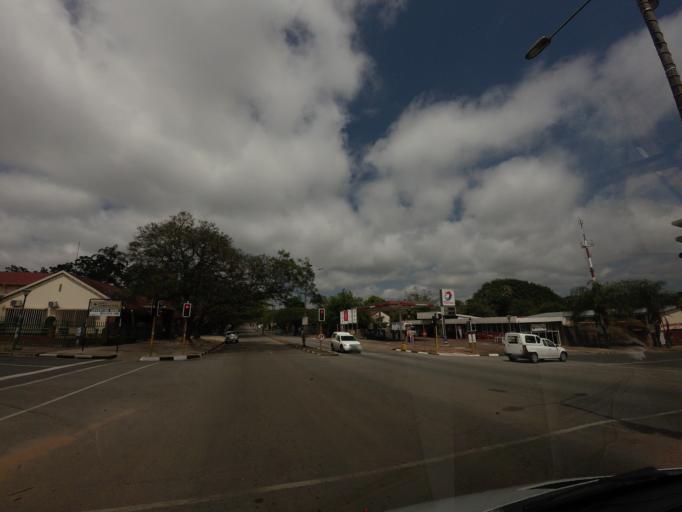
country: ZA
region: Mpumalanga
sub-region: Ehlanzeni District
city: White River
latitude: -25.3284
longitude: 31.0192
